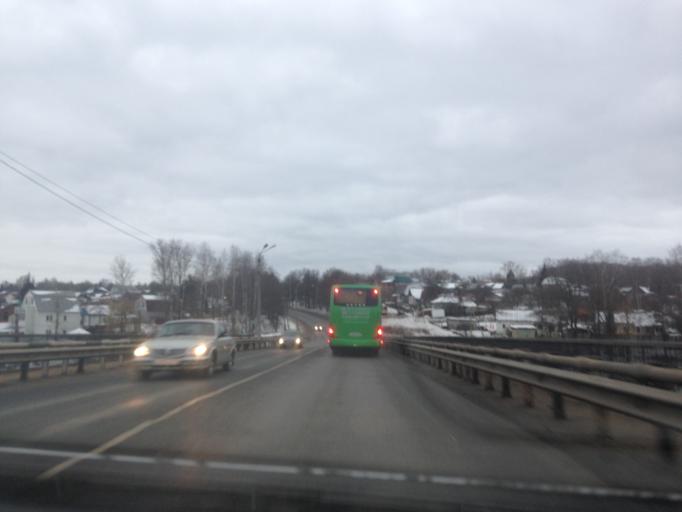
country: RU
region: Tula
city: Kosaya Gora
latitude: 54.1171
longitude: 37.5630
